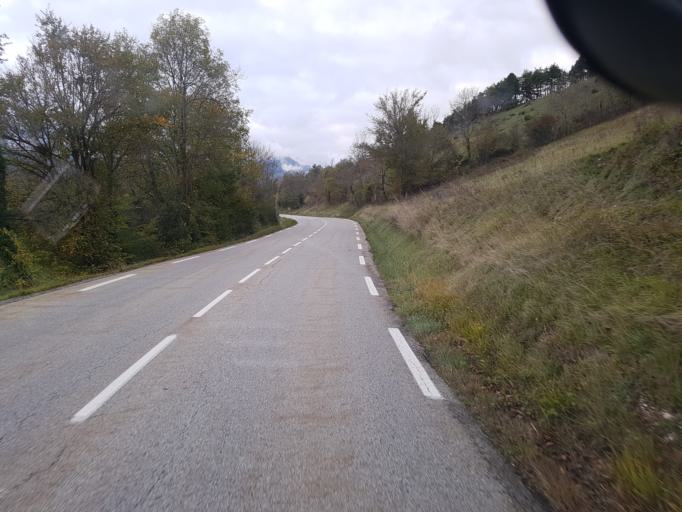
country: FR
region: Rhone-Alpes
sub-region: Departement de l'Isere
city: Le Gua
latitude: 44.9605
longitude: 5.6369
